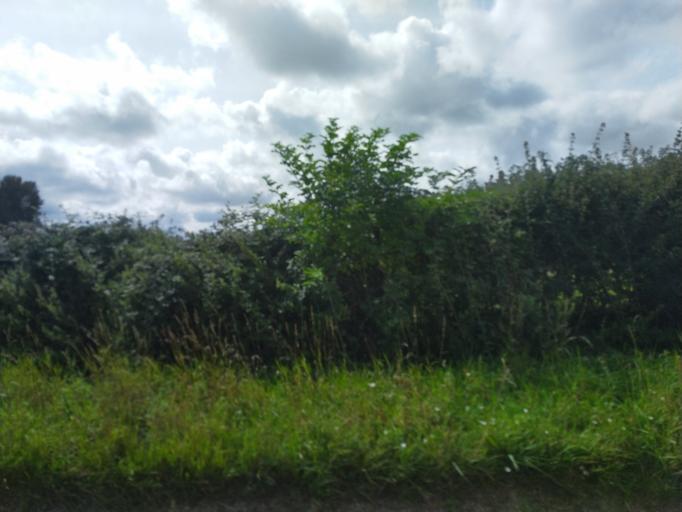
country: GB
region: England
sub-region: Dorset
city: Lytchett Matravers
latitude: 50.7947
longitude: -2.1149
